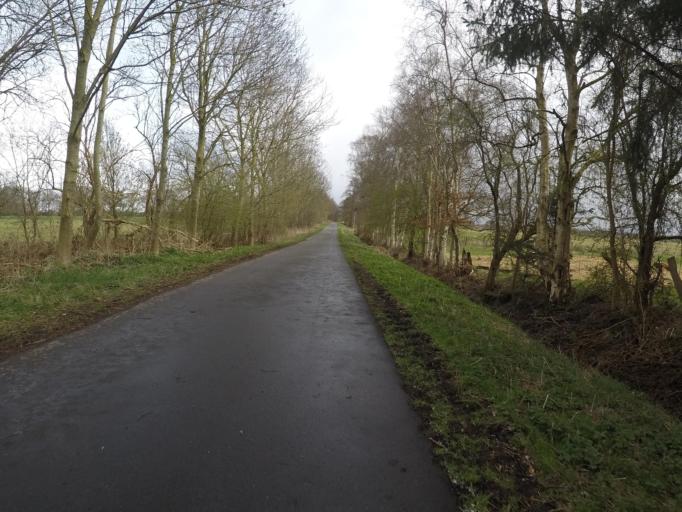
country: DE
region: Lower Saxony
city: Elmlohe
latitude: 53.5992
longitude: 8.6879
